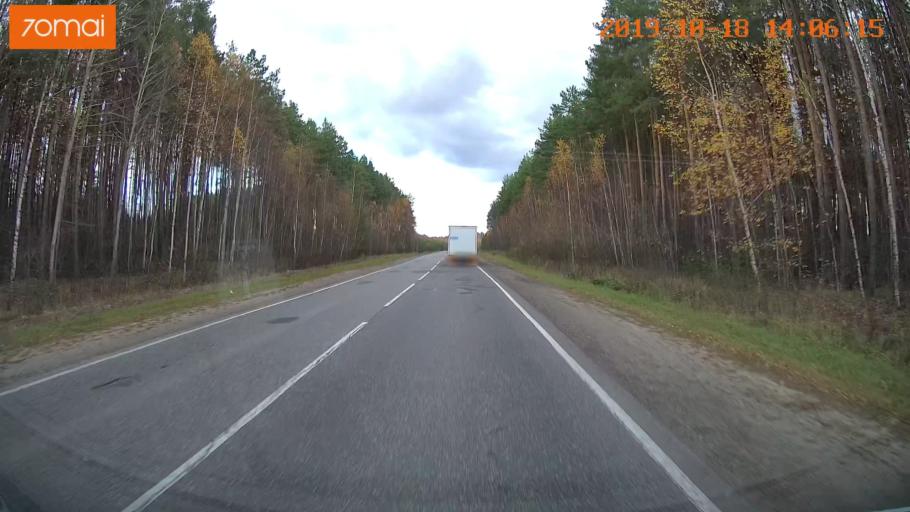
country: RU
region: Rjazan
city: Spas-Klepiki
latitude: 55.1430
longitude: 40.1495
